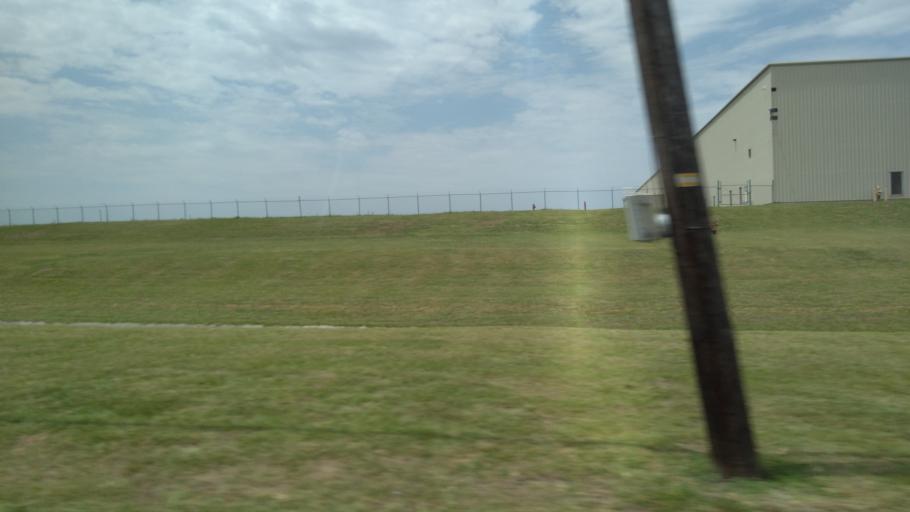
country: US
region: Texas
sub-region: McLennan County
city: Beverly Hills
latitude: 31.4916
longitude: -97.1638
